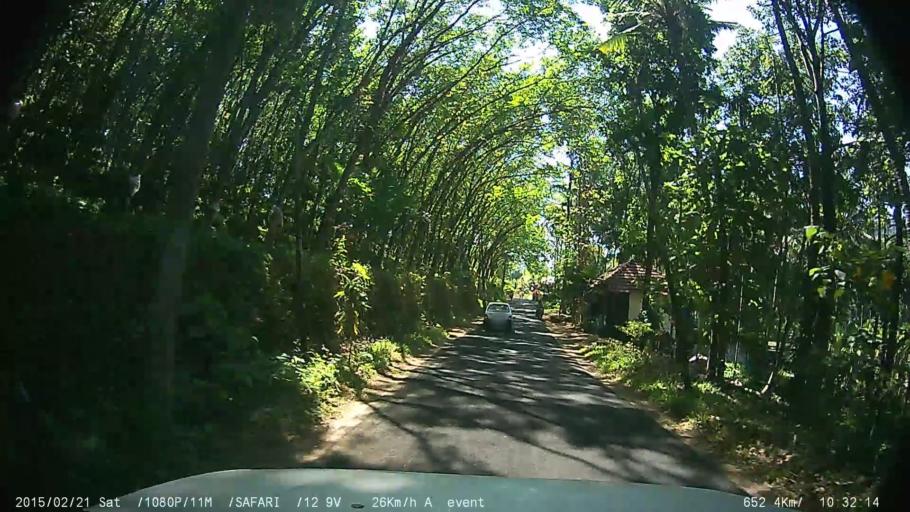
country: IN
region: Kerala
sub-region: Kottayam
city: Lalam
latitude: 9.8407
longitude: 76.7096
